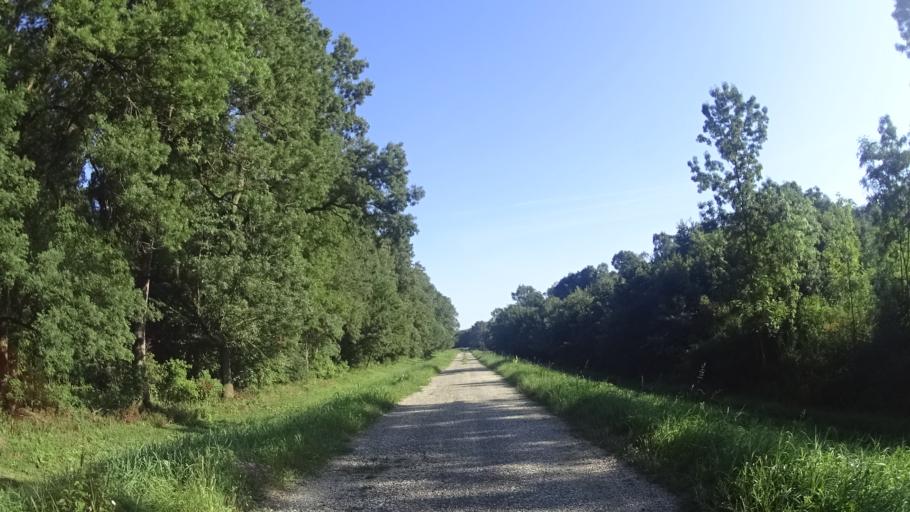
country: AT
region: Lower Austria
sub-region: Politischer Bezirk Mistelbach
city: Rabensburg
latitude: 48.6391
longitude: 16.9783
